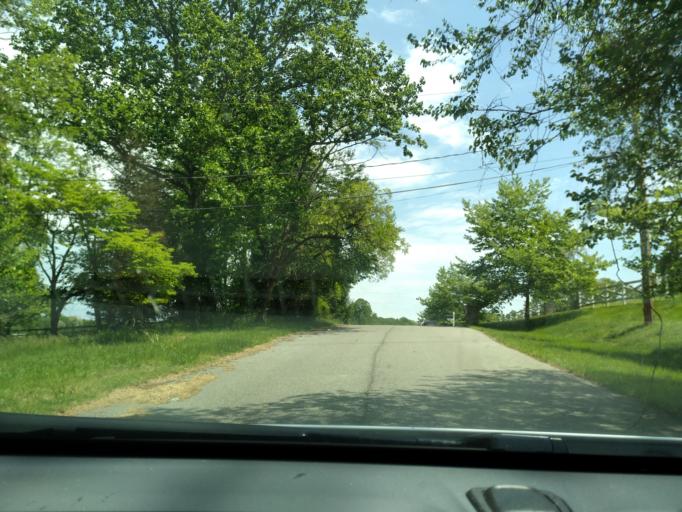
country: US
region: Maryland
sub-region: Prince George's County
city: Marlboro Meadows
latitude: 38.8529
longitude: -76.7141
